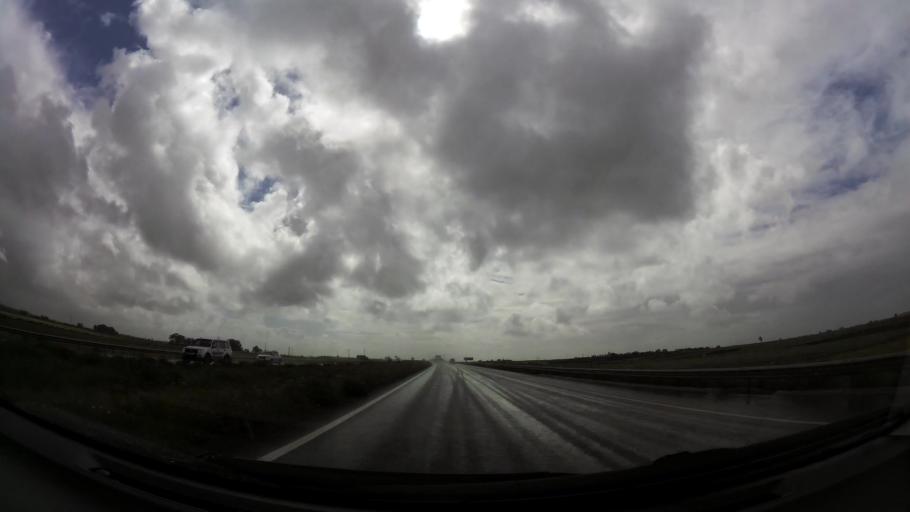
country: MA
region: Grand Casablanca
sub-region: Nouaceur
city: Dar Bouazza
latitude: 33.3756
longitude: -7.9093
